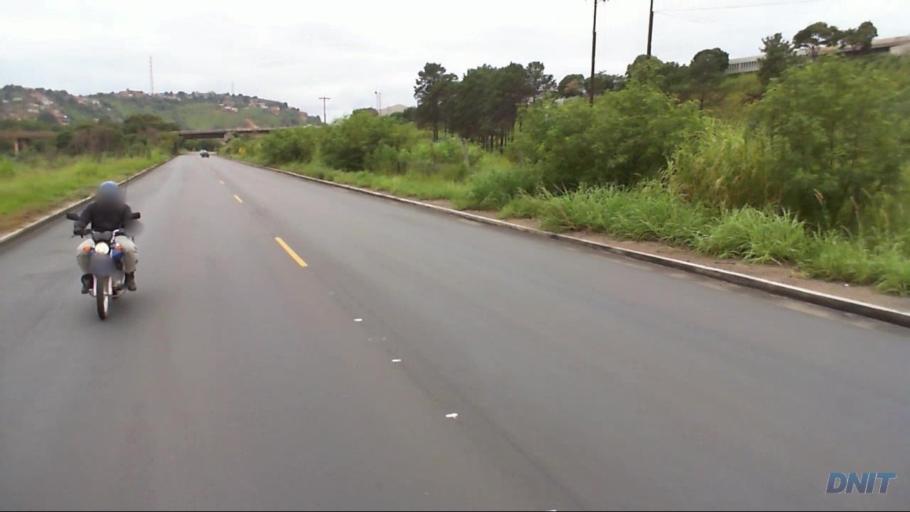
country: BR
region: Minas Gerais
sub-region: Coronel Fabriciano
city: Coronel Fabriciano
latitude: -19.5253
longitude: -42.6430
